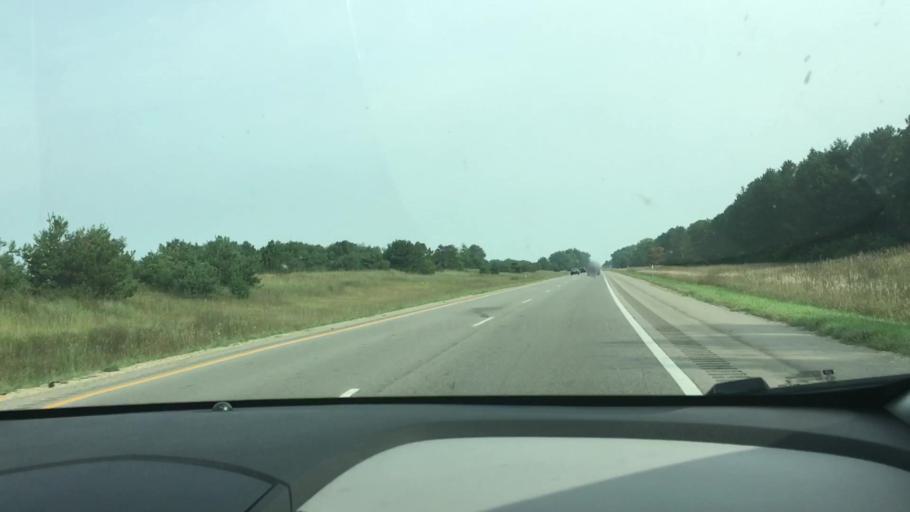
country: US
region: Michigan
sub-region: Kalamazoo County
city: Schoolcraft
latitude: 42.1586
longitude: -85.6439
